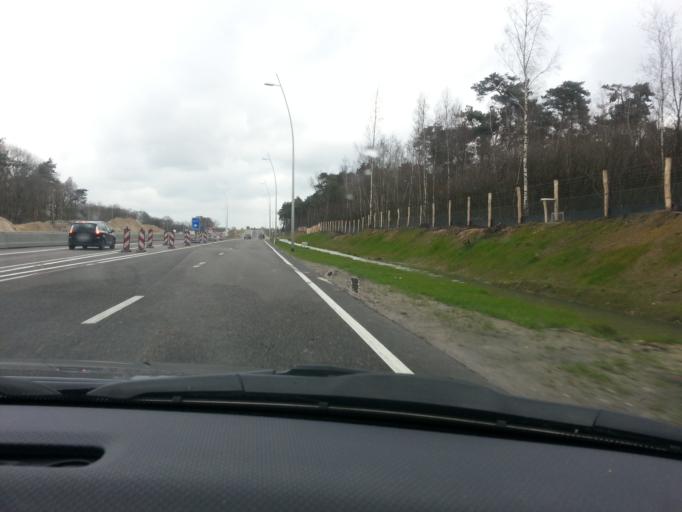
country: NL
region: North Brabant
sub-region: Gemeente Loon op Zand
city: Loon op Zand
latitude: 51.6504
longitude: 5.0571
